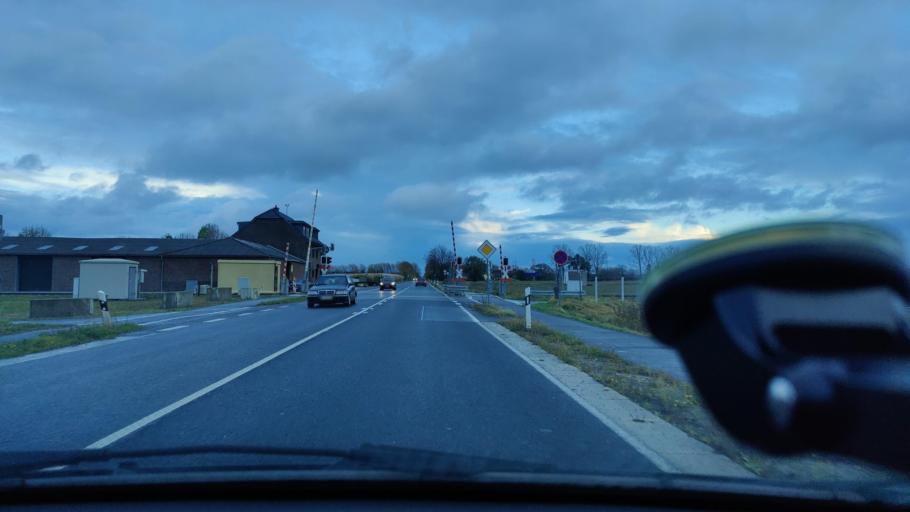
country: DE
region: North Rhine-Westphalia
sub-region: Regierungsbezirk Koln
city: Wurselen
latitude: 50.8245
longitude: 6.1921
